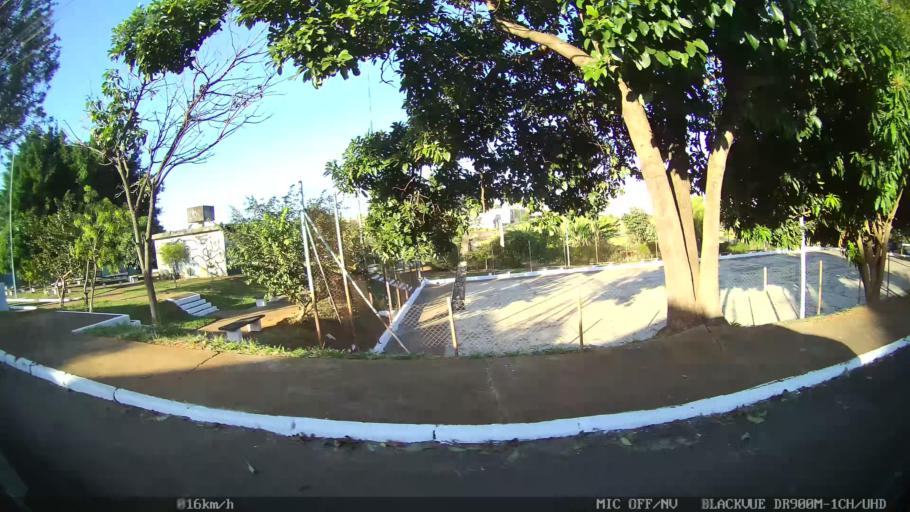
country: BR
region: Sao Paulo
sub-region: Franca
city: Franca
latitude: -20.5334
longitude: -47.3779
